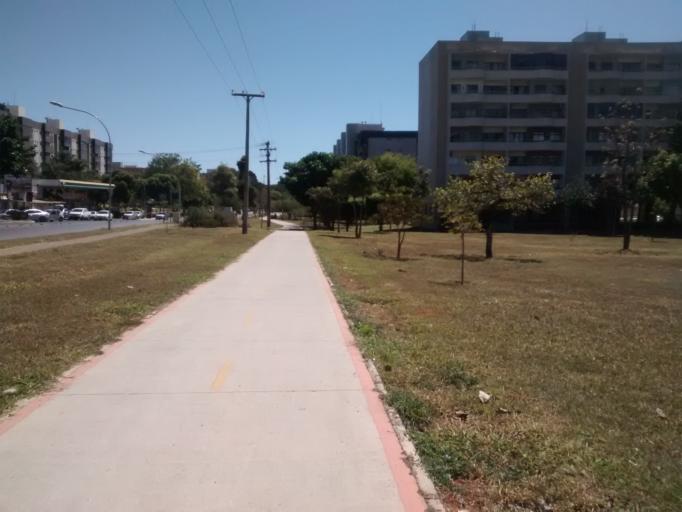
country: BR
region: Federal District
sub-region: Brasilia
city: Brasilia
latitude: -15.7562
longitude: -47.8895
